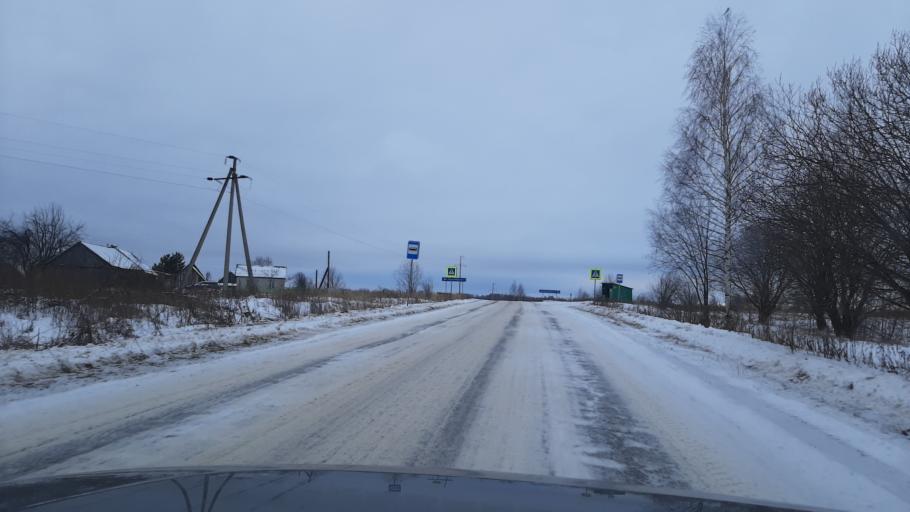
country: RU
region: Kostroma
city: Volgorechensk
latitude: 57.4389
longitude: 41.0925
